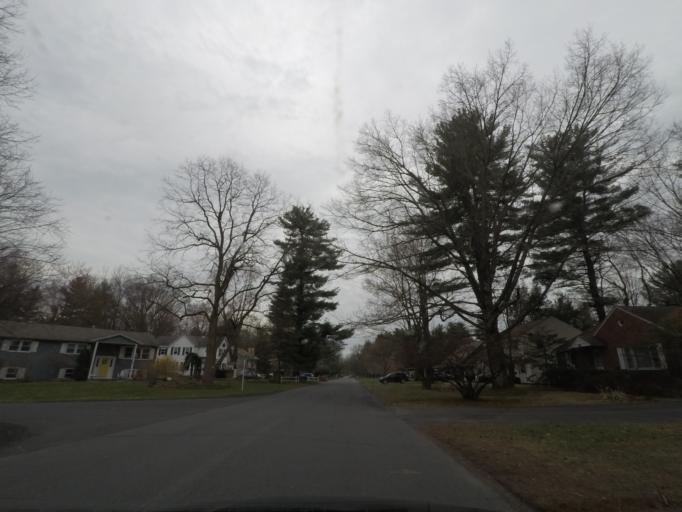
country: US
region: New York
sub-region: Albany County
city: Delmar
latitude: 42.6085
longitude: -73.8373
